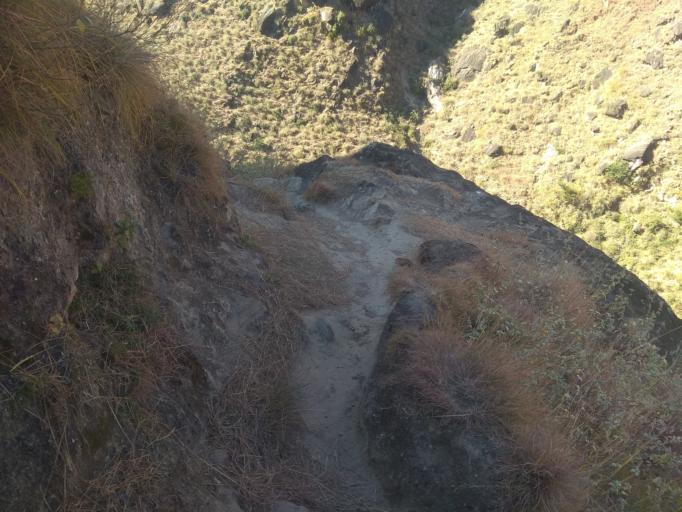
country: NP
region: Mid Western
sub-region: Bheri Zone
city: Dailekh
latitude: 29.2561
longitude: 81.6745
